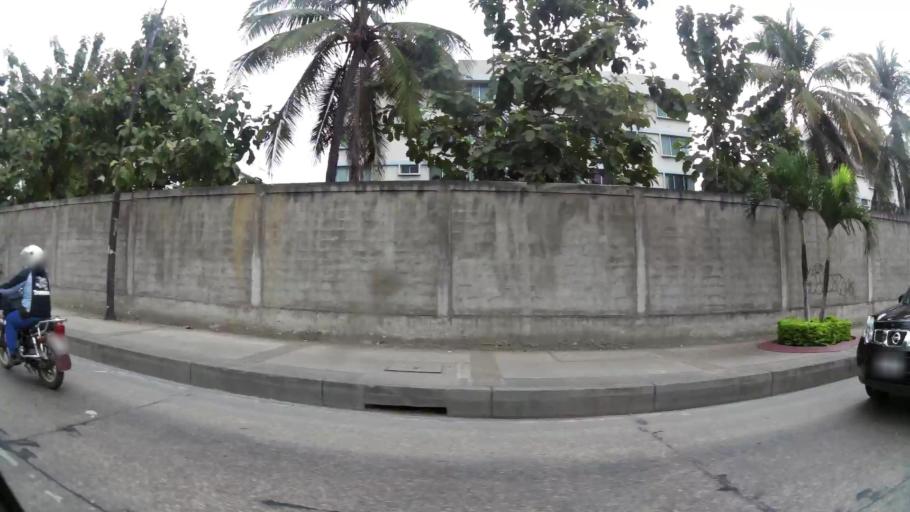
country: EC
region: Guayas
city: Eloy Alfaro
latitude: -2.1676
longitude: -79.8800
